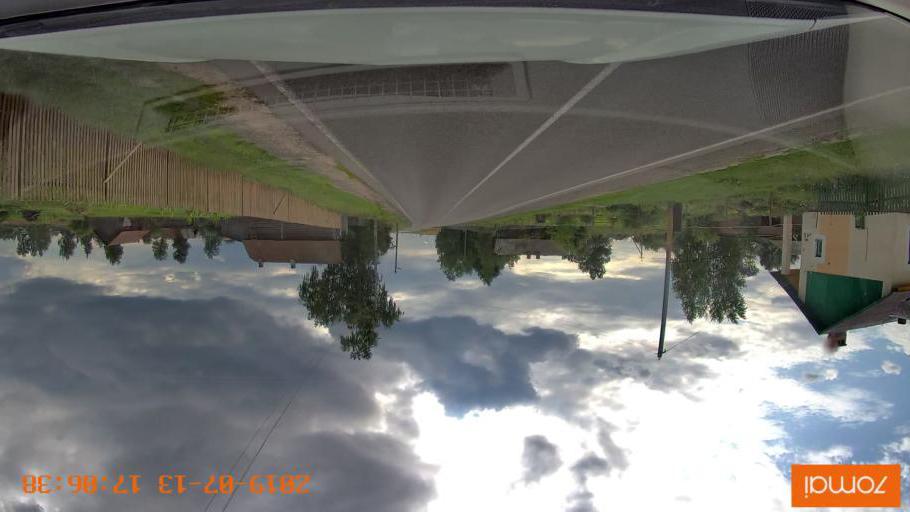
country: BY
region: Mogilev
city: Kirawsk
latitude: 53.2681
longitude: 29.3475
